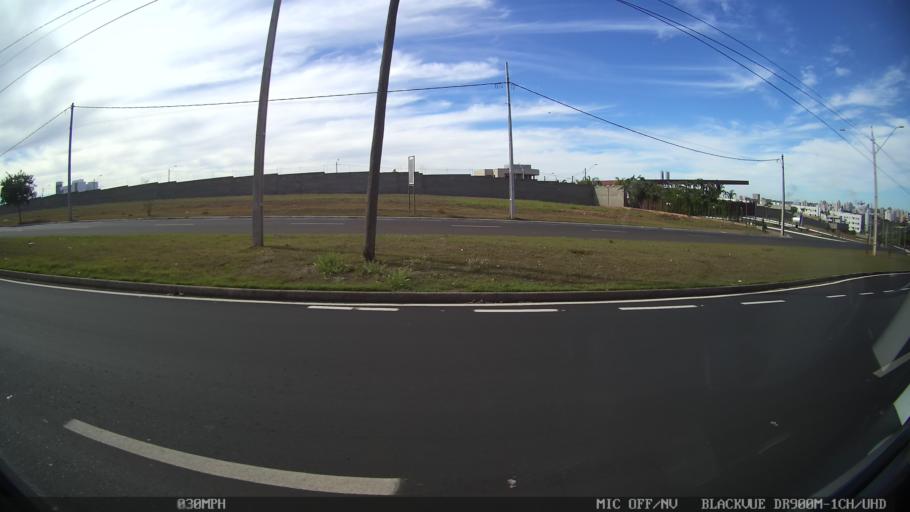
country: BR
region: Sao Paulo
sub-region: Catanduva
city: Catanduva
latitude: -21.1175
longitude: -48.9786
